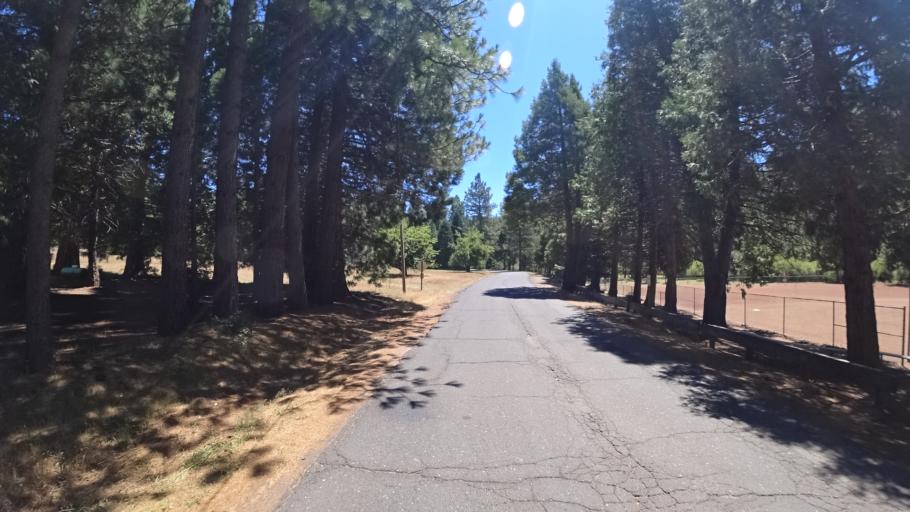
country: US
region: California
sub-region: Calaveras County
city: Arnold
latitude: 38.2356
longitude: -120.3413
